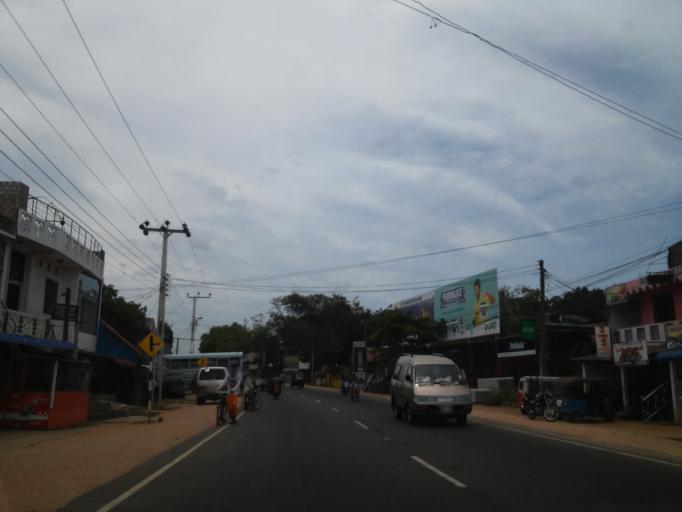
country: LK
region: Eastern Province
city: Trincomalee
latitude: 8.5862
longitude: 81.2099
